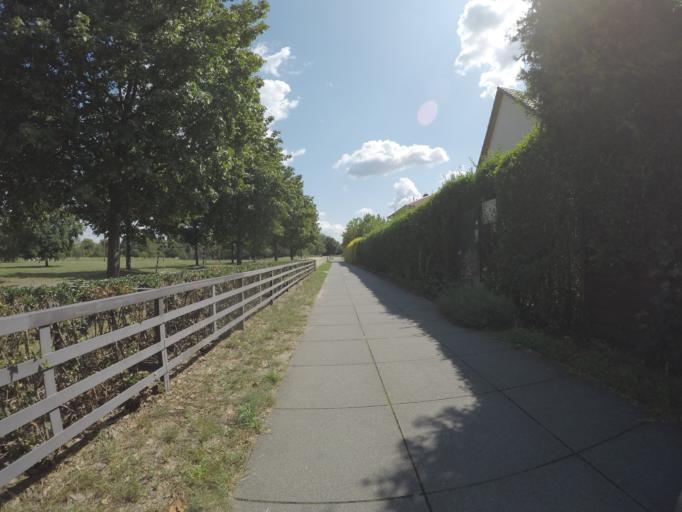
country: DE
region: Berlin
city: Biesdorf
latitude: 52.5003
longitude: 13.5680
